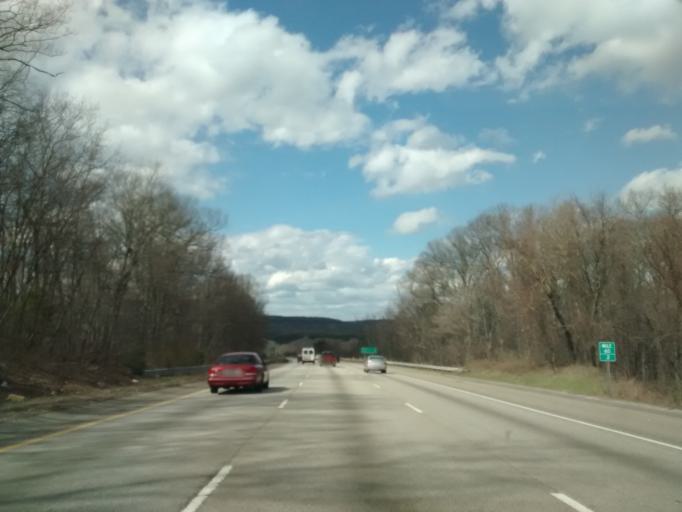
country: US
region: Massachusetts
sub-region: Worcester County
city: Southborough
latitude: 42.2994
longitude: -71.5652
